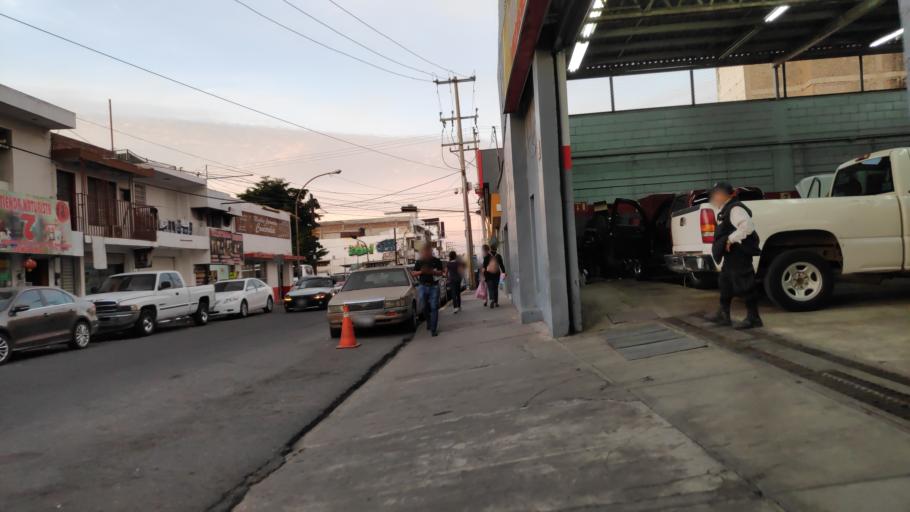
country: MX
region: Sinaloa
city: Culiacan
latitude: 24.8040
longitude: -107.3958
